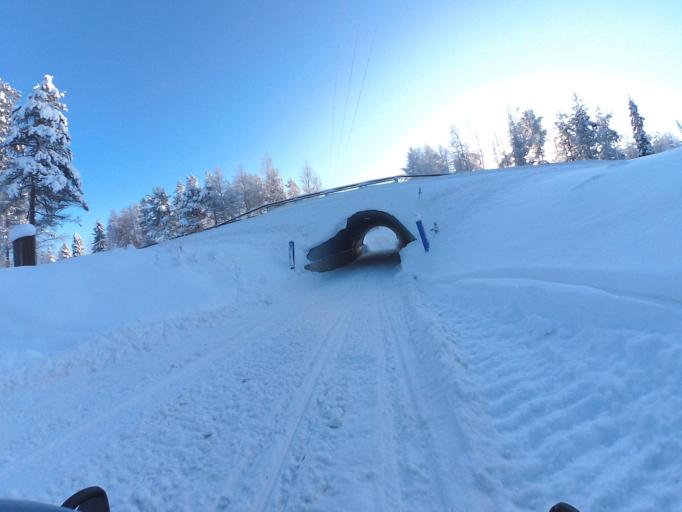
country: FI
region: Lapland
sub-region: Rovaniemi
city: Rovaniemi
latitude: 66.5470
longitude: 25.8615
